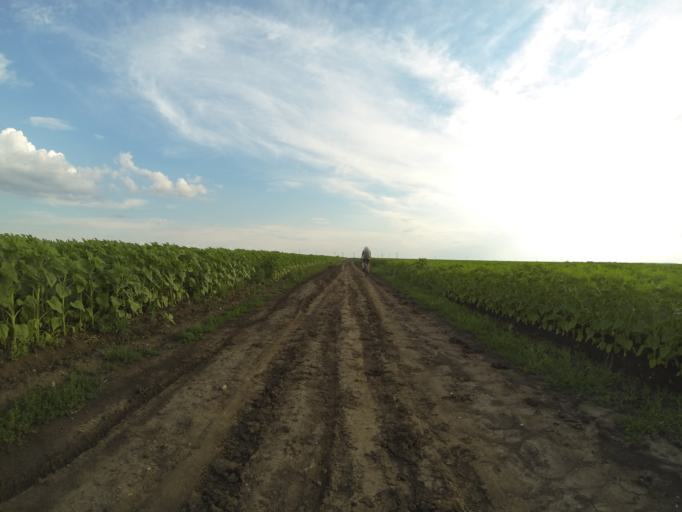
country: RO
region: Dolj
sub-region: Comuna Caloparu
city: Salcuta
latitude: 44.1383
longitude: 23.6897
